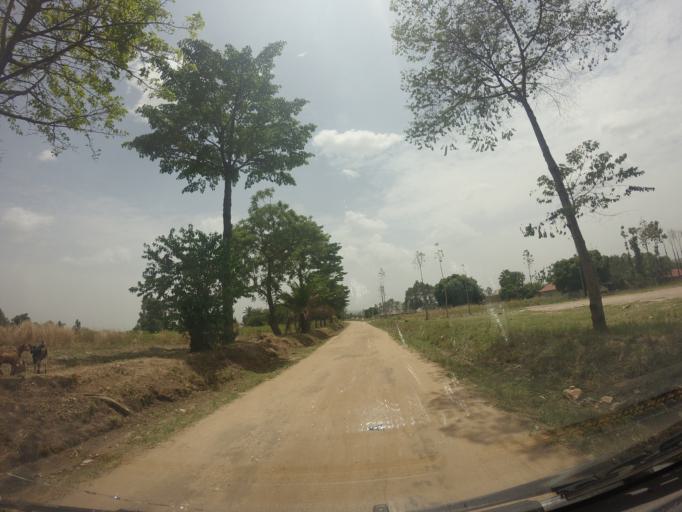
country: UG
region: Northern Region
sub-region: Arua District
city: Arua
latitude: 2.9460
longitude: 30.9131
